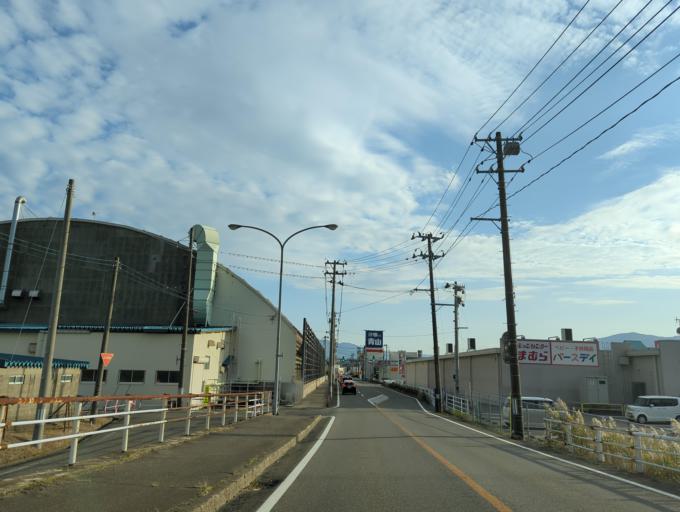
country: JP
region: Niigata
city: Kashiwazaki
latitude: 37.3635
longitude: 138.5635
